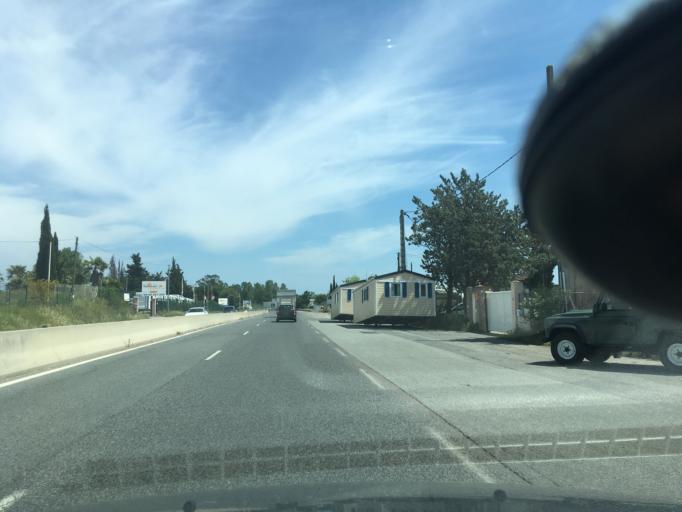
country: FR
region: Provence-Alpes-Cote d'Azur
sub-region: Departement du Var
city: Roquebrune-sur-Argens
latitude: 43.4632
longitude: 6.6425
